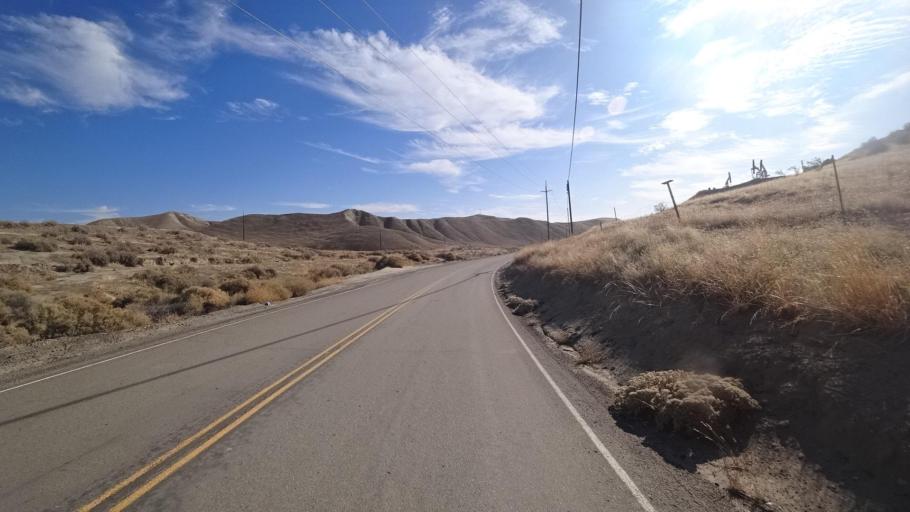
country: US
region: California
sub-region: Kern County
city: Oildale
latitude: 35.5663
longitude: -118.9568
